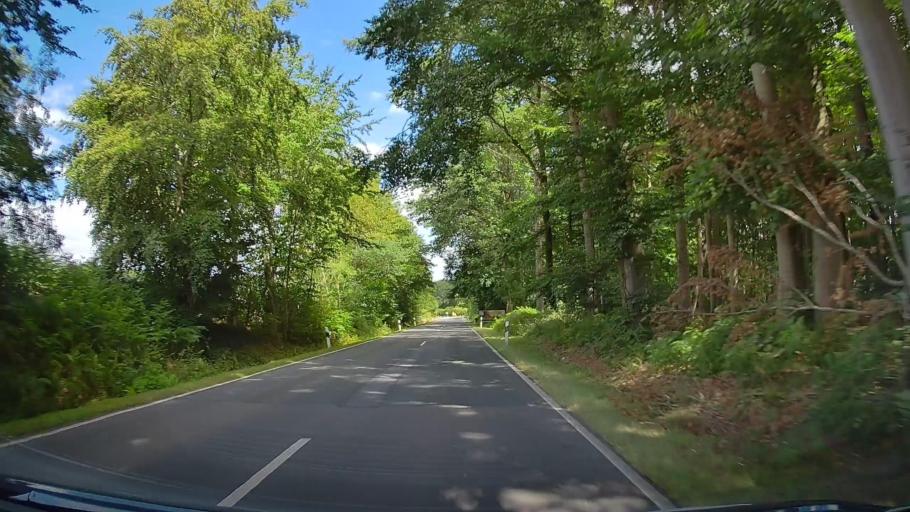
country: DE
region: Lower Saxony
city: Belm
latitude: 52.3665
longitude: 8.1461
